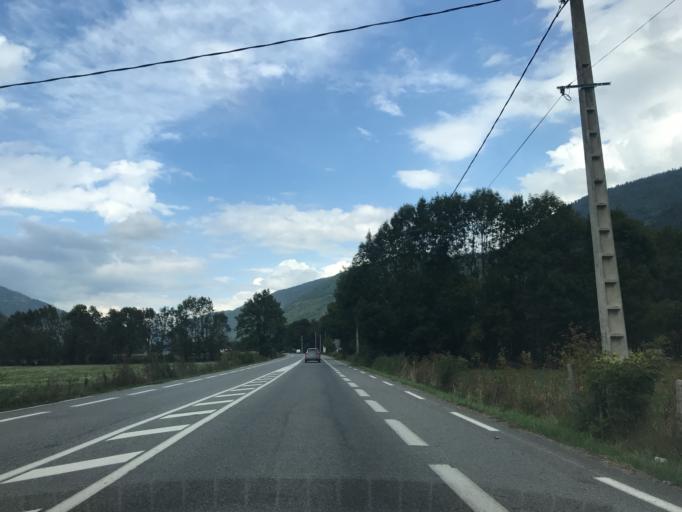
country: FR
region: Midi-Pyrenees
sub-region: Departement des Hautes-Pyrenees
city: Saint-Lary-Soulan
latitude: 42.8347
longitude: 0.3408
